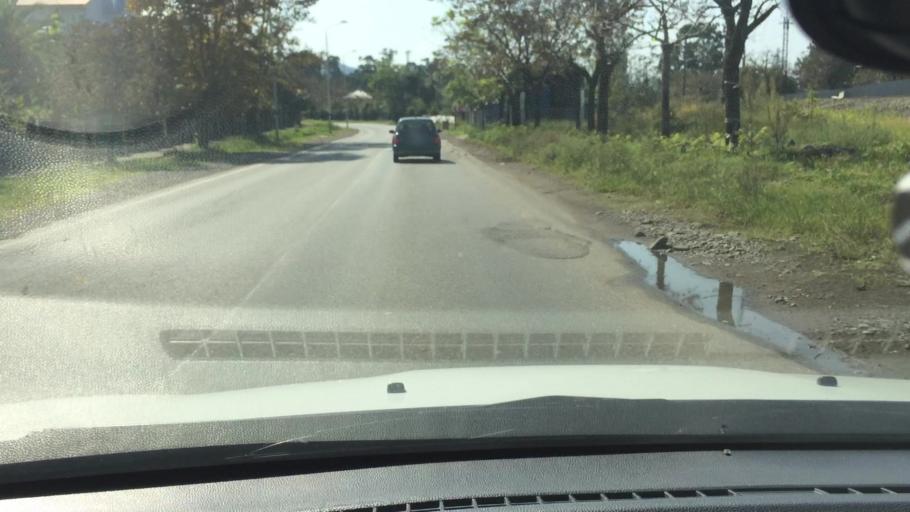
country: GE
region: Ajaria
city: Makhinjauri
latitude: 41.7293
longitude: 41.7313
